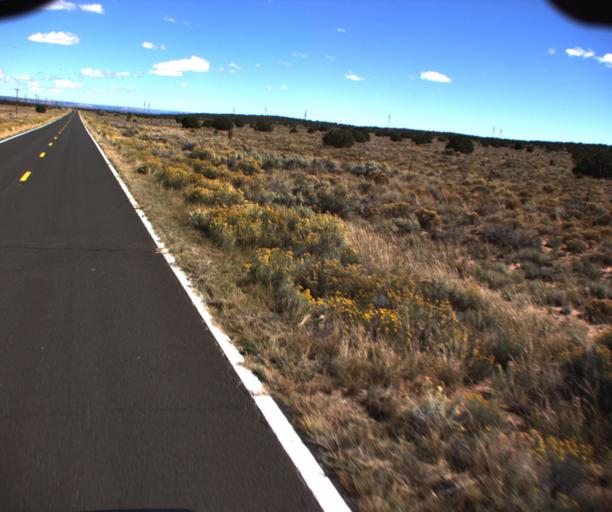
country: US
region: New Mexico
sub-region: McKinley County
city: Zuni Pueblo
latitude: 35.0119
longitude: -109.0656
